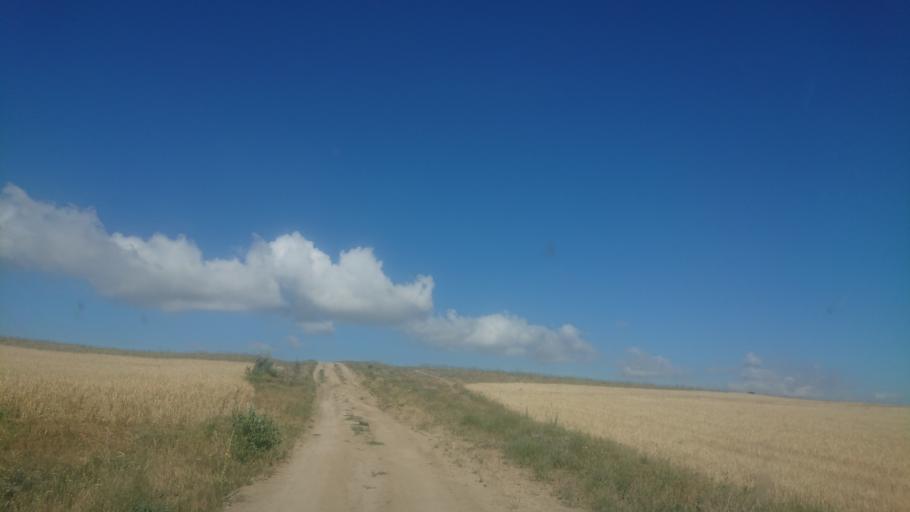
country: TR
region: Aksaray
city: Agacoren
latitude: 38.9103
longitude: 33.8748
